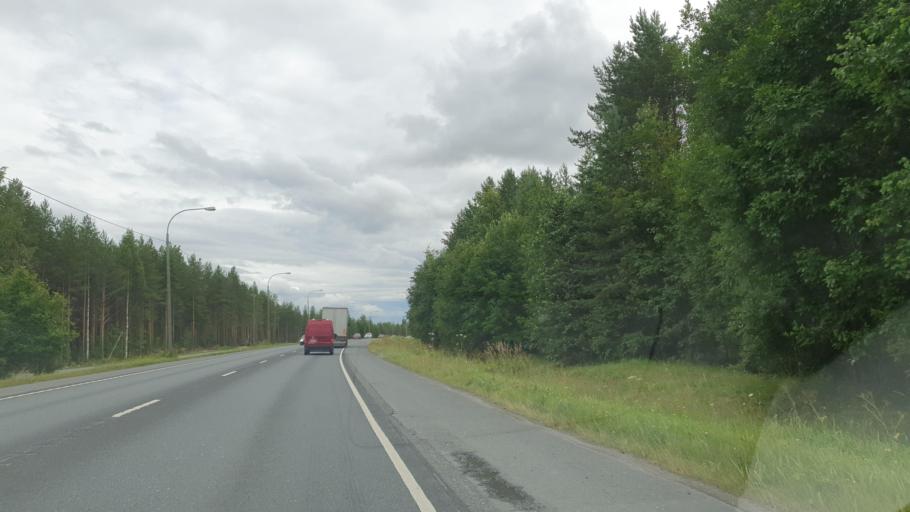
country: FI
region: Northern Savo
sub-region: Ylae-Savo
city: Iisalmi
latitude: 63.4892
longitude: 27.2837
